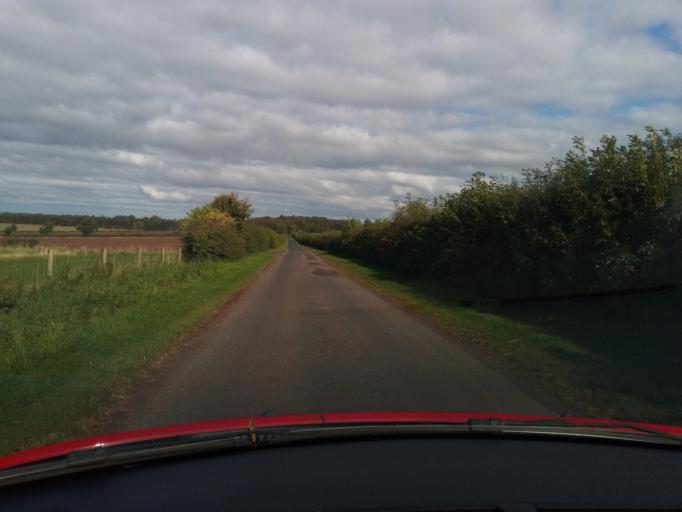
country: GB
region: Scotland
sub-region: The Scottish Borders
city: Kelso
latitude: 55.5734
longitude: -2.4068
